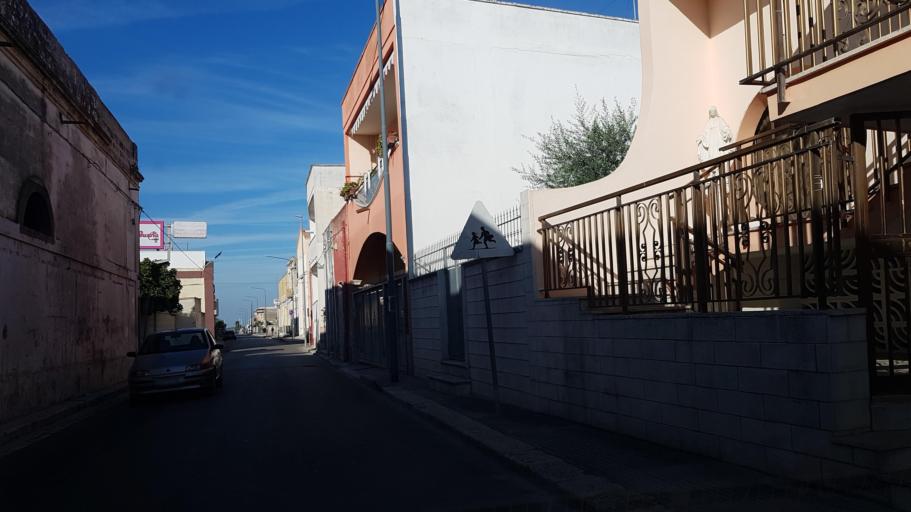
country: IT
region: Apulia
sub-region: Provincia di Lecce
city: Salice Salentino
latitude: 40.3855
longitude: 17.9659
